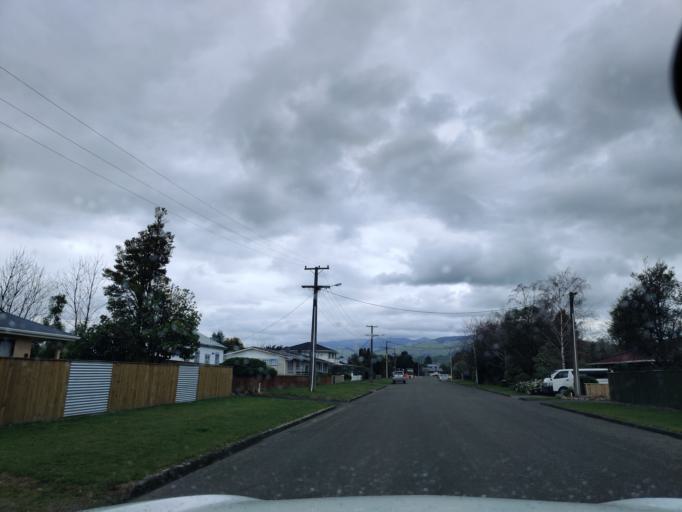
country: NZ
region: Manawatu-Wanganui
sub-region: Palmerston North City
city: Palmerston North
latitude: -40.2870
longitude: 175.7502
